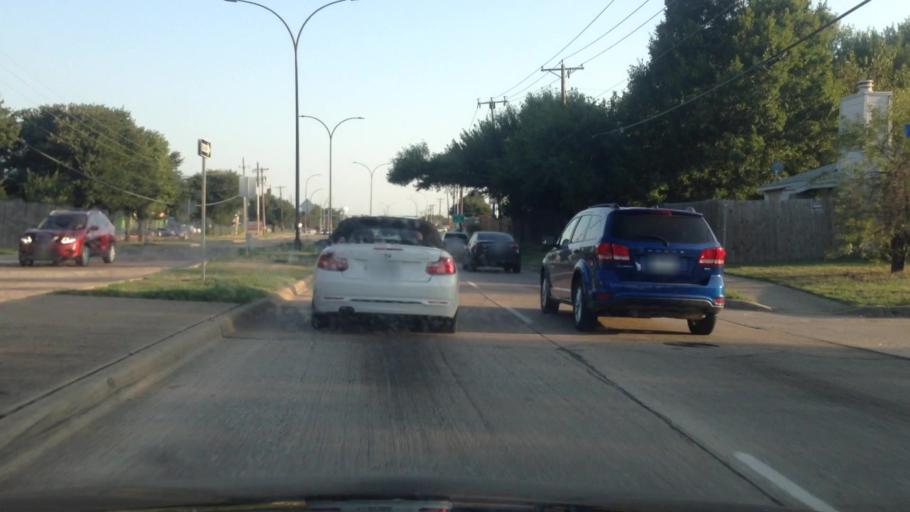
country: US
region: Texas
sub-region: Tarrant County
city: Dalworthington Gardens
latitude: 32.6625
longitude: -97.1151
